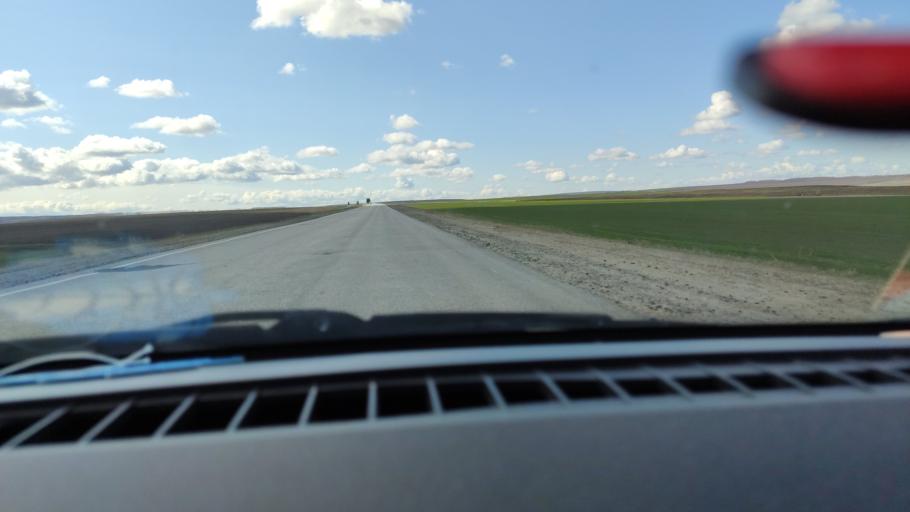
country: RU
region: Samara
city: Varlamovo
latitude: 53.0390
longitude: 48.3381
